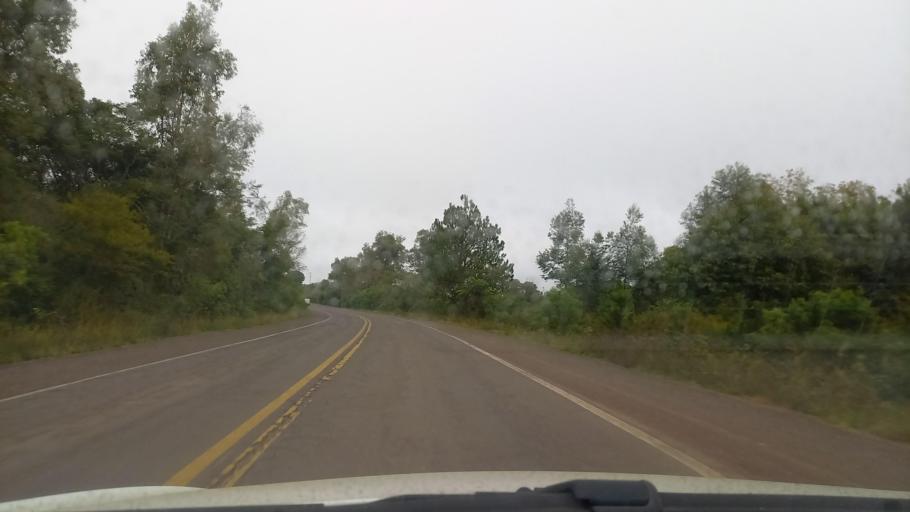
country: BR
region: Rio Grande do Sul
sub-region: Cacequi
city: Cacequi
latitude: -30.0875
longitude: -54.6269
